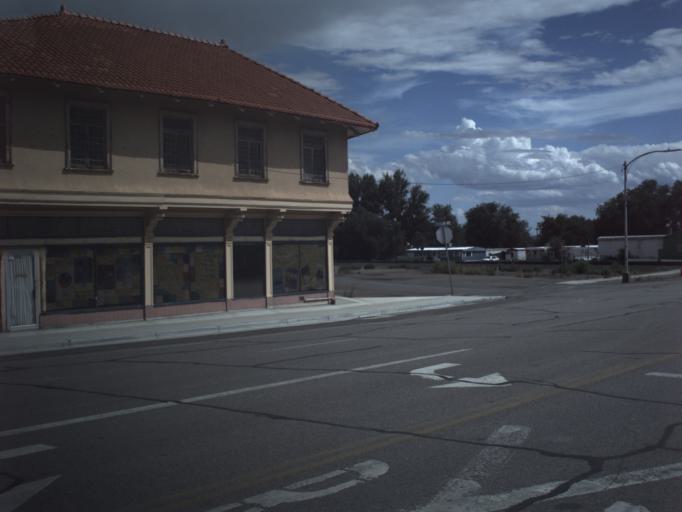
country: US
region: Utah
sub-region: Carbon County
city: Price
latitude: 39.5980
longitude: -110.8113
